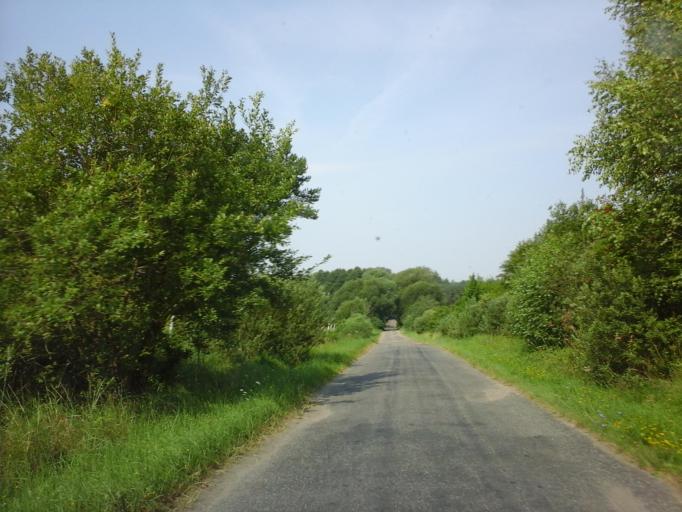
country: PL
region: West Pomeranian Voivodeship
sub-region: Powiat mysliborski
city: Barlinek
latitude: 53.0675
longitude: 15.2292
